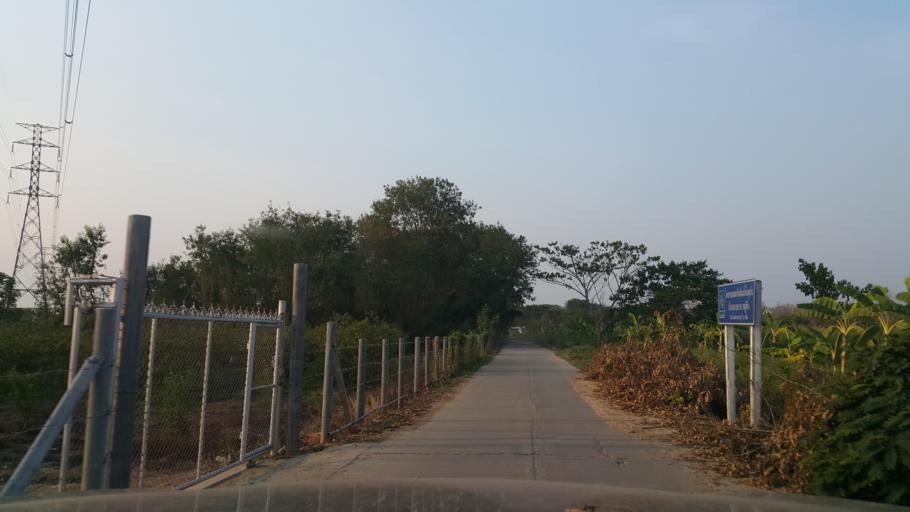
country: TH
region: Chiang Mai
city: Saraphi
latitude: 18.7214
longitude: 99.0161
